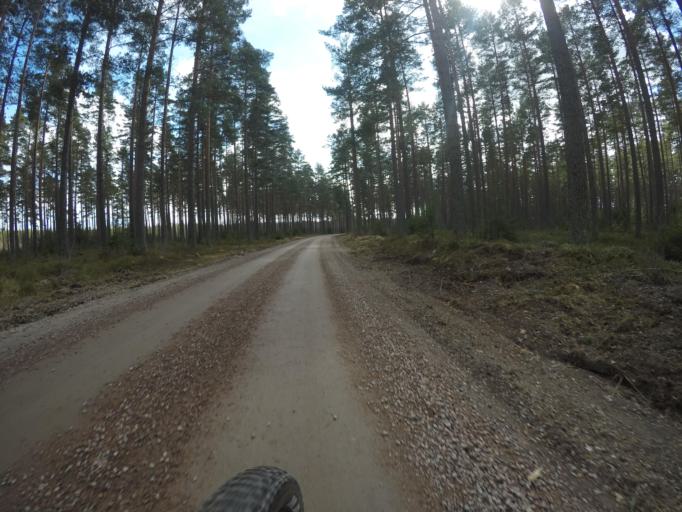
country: SE
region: Vaestmanland
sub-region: Kungsors Kommun
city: Kungsoer
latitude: 59.3705
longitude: 16.1007
